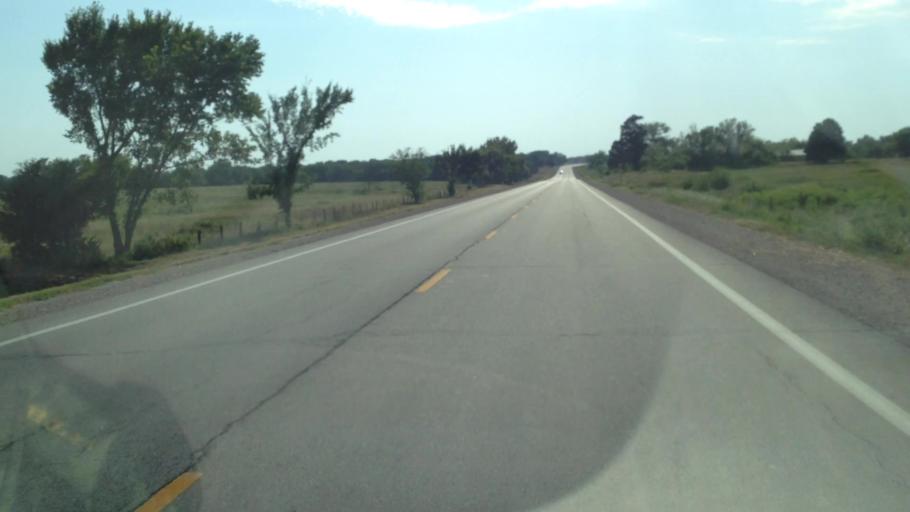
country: US
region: Kansas
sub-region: Anderson County
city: Garnett
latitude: 38.0817
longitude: -95.2293
